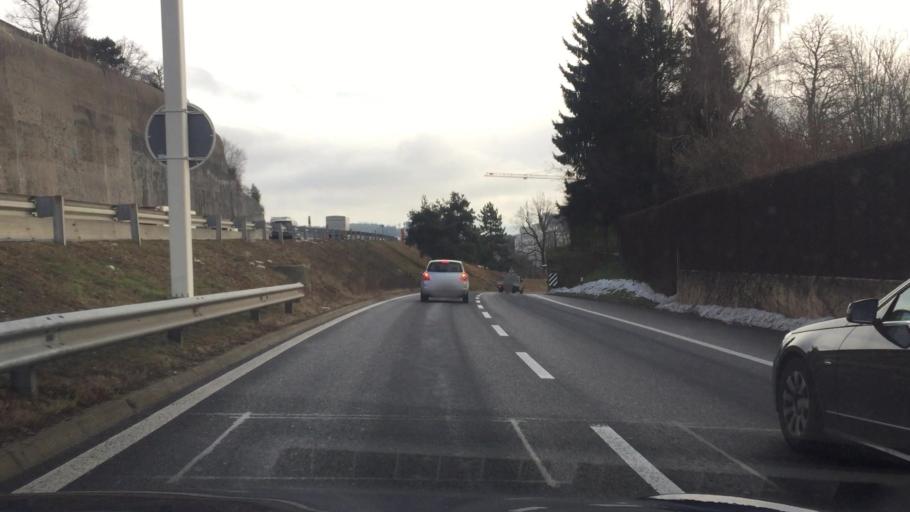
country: CH
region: Vaud
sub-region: Lausanne District
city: Epalinges
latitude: 46.5421
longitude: 6.6503
